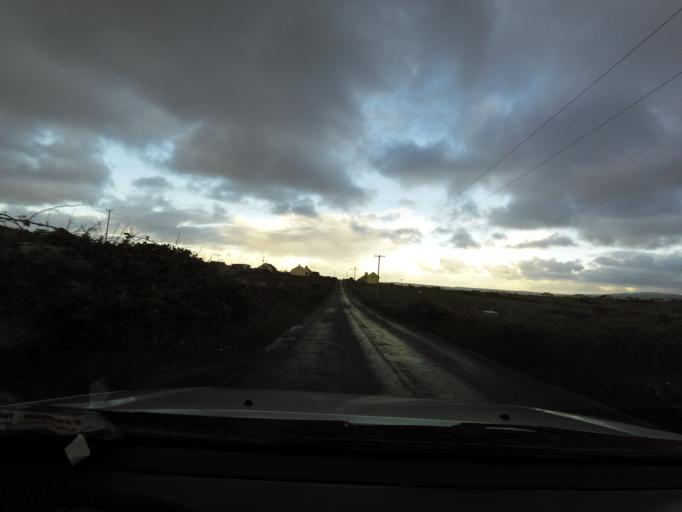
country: IE
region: Munster
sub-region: An Clar
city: Kilrush
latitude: 52.9432
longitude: -9.4138
